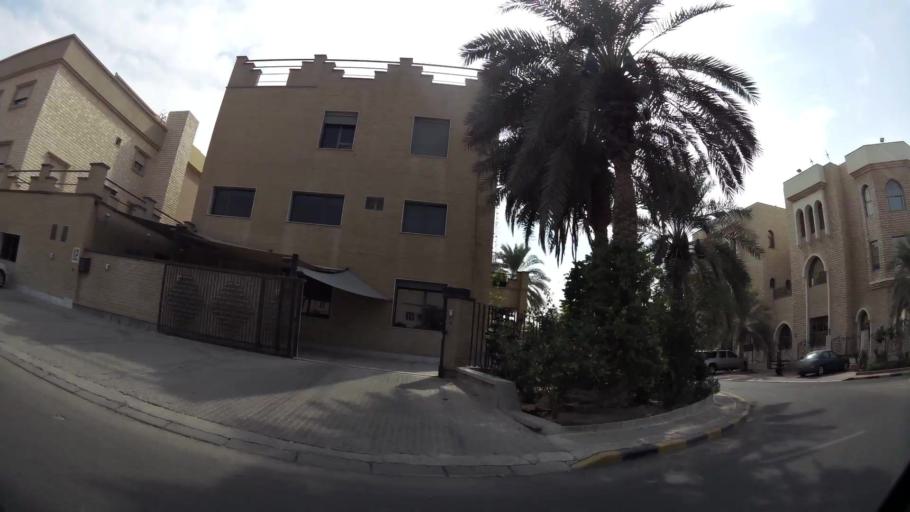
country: KW
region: Al Asimah
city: Ash Shamiyah
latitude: 29.3362
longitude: 47.9693
